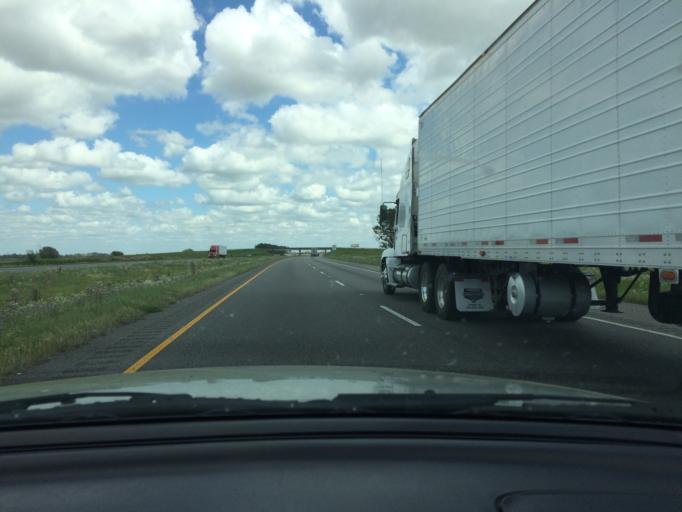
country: US
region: Louisiana
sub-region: Jefferson Davis Parish
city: Jennings
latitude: 30.2475
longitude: -92.7293
